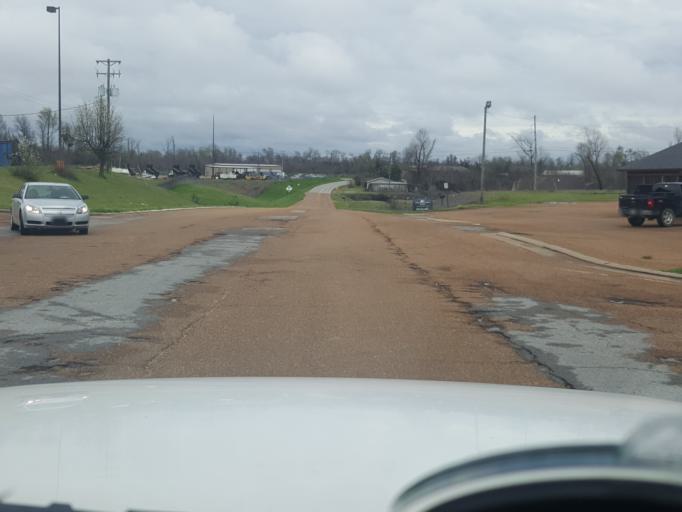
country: US
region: Mississippi
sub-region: Yazoo County
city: Yazoo City
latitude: 32.8399
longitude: -90.3857
